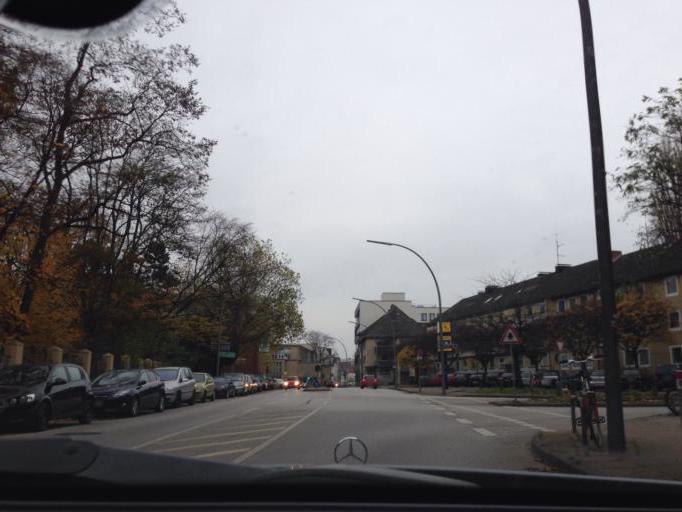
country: DE
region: Hamburg
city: Marienthal
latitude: 53.5747
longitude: 10.0671
